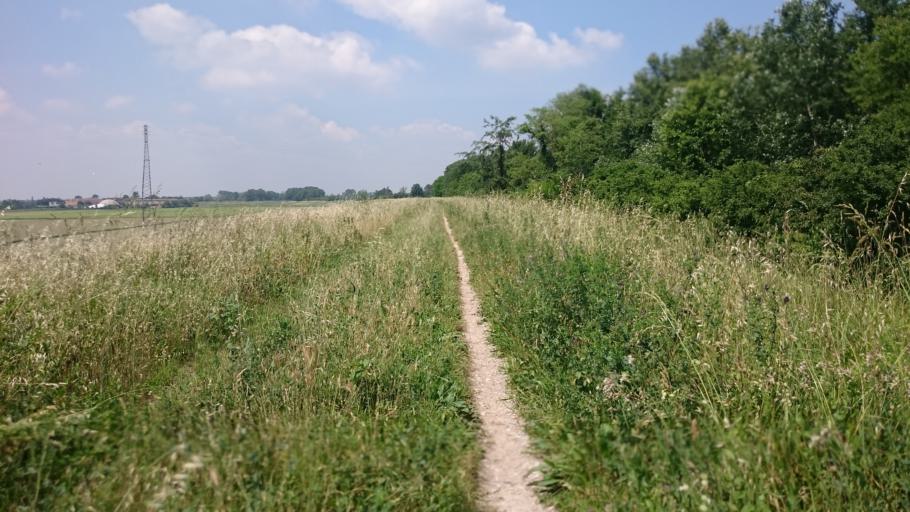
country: IT
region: Lombardy
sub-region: Provincia di Mantova
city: San Biagio
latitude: 45.1236
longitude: 10.8493
